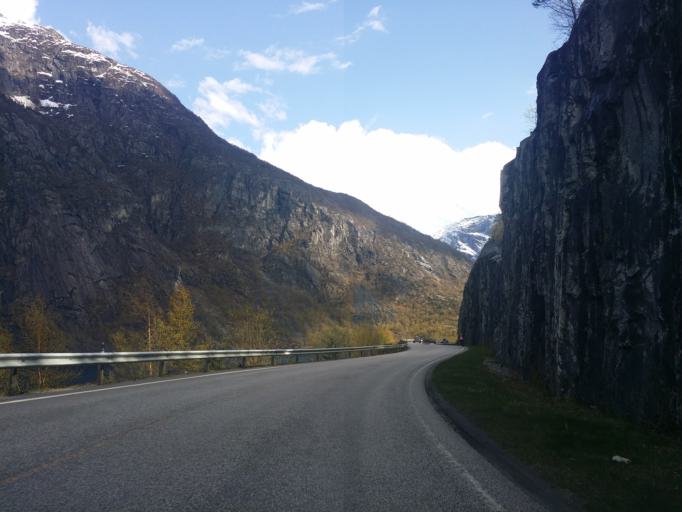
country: NO
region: Hordaland
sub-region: Eidfjord
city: Eidfjord
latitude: 60.4463
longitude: 7.1027
